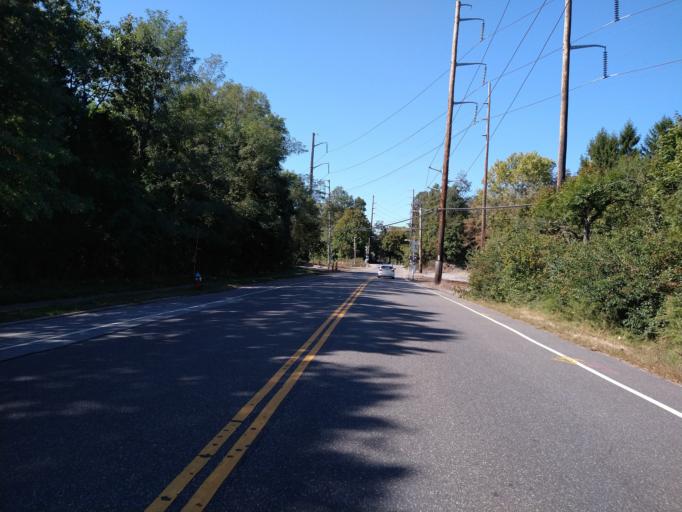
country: US
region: New York
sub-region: Nassau County
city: Syosset
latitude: 40.8262
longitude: -73.4891
